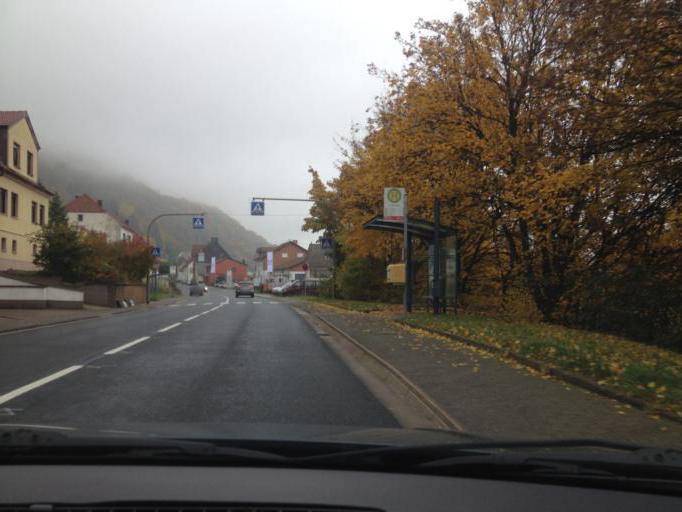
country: DE
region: Saarland
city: Tholey
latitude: 49.4799
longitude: 7.0245
